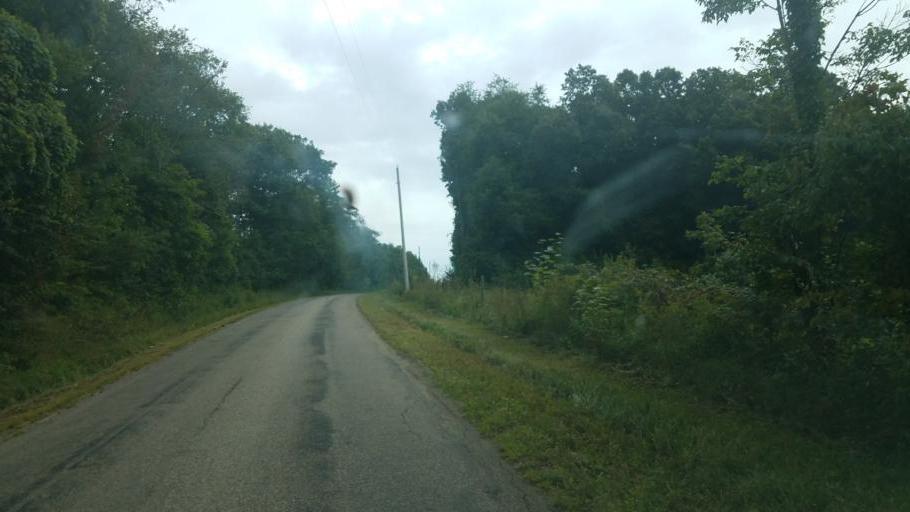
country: US
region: Ohio
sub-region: Sandusky County
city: Bellville
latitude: 40.5650
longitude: -82.3801
